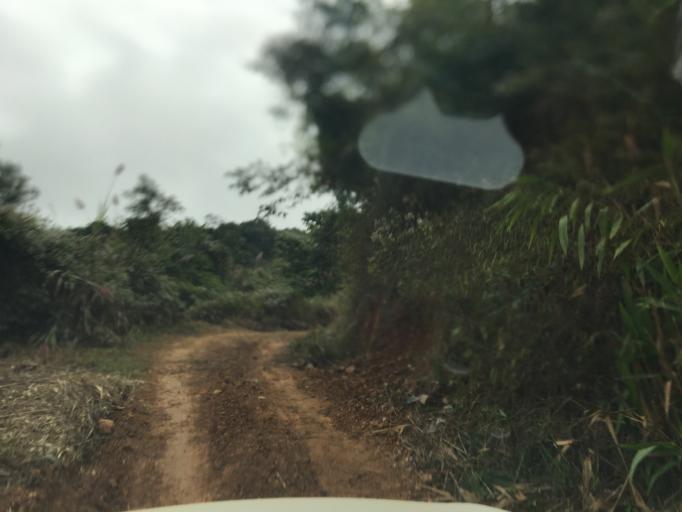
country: LA
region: Houaphan
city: Viengthong
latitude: 19.9384
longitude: 103.2991
